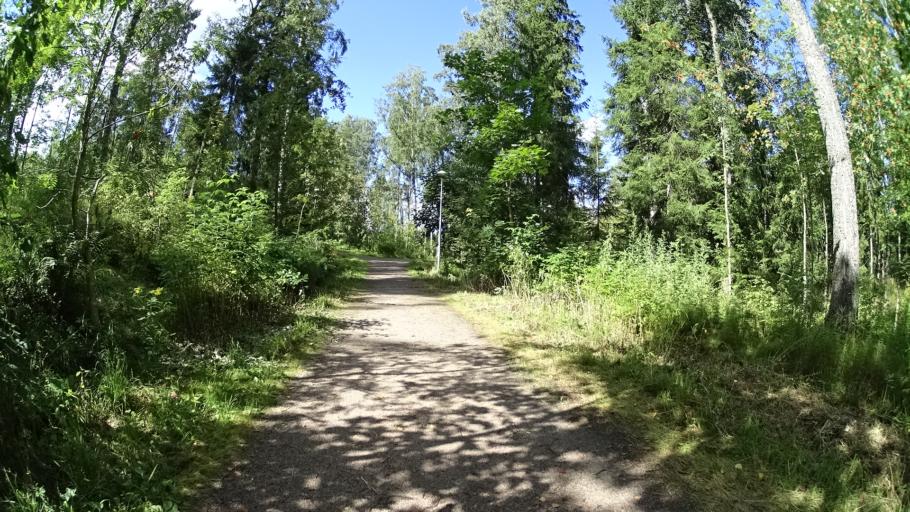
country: FI
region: Uusimaa
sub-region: Helsinki
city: Kauniainen
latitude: 60.2316
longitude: 24.7484
